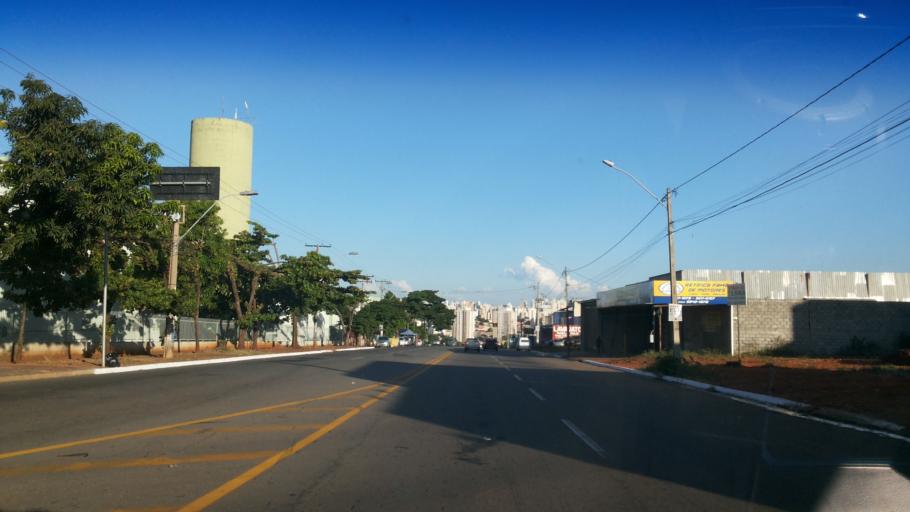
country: BR
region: Goias
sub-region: Goiania
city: Goiania
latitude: -16.6431
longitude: -49.2787
